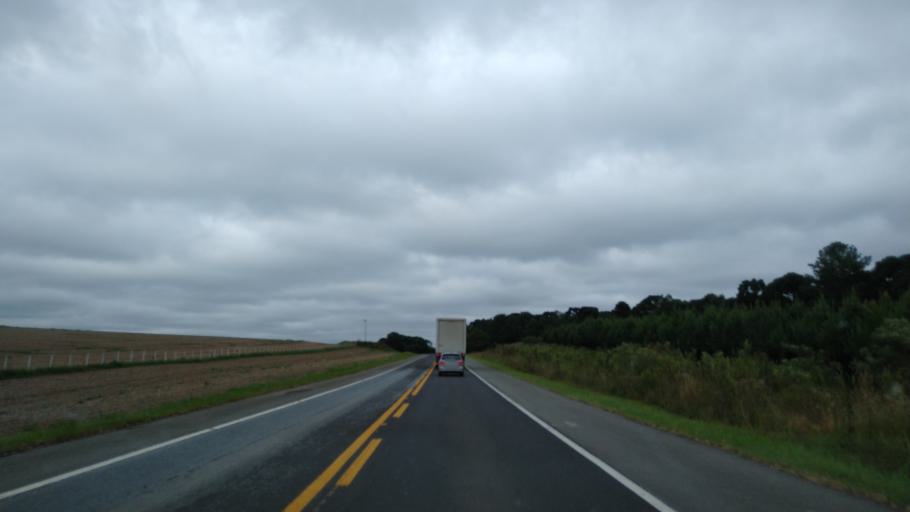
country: BR
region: Santa Catarina
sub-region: Tres Barras
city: Tres Barras
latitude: -26.1694
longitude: -50.0943
